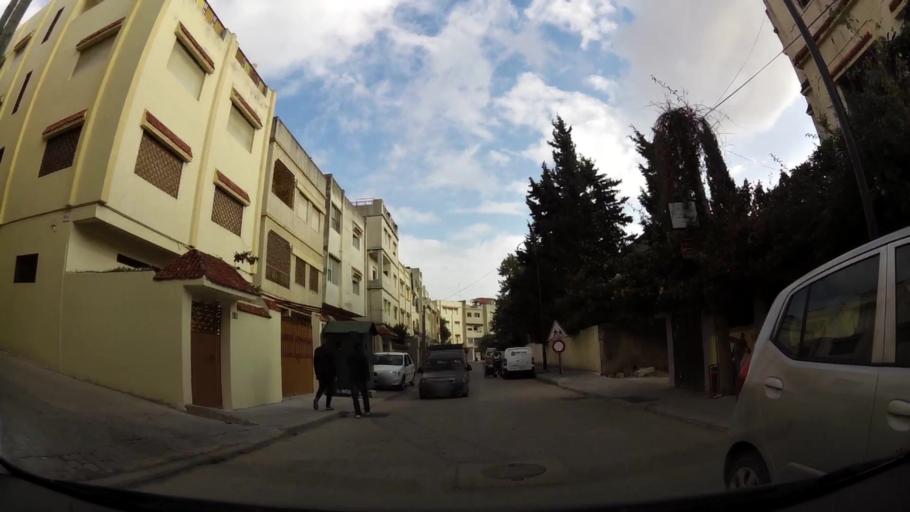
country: MA
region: Tanger-Tetouan
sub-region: Tanger-Assilah
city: Tangier
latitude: 35.7614
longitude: -5.8314
